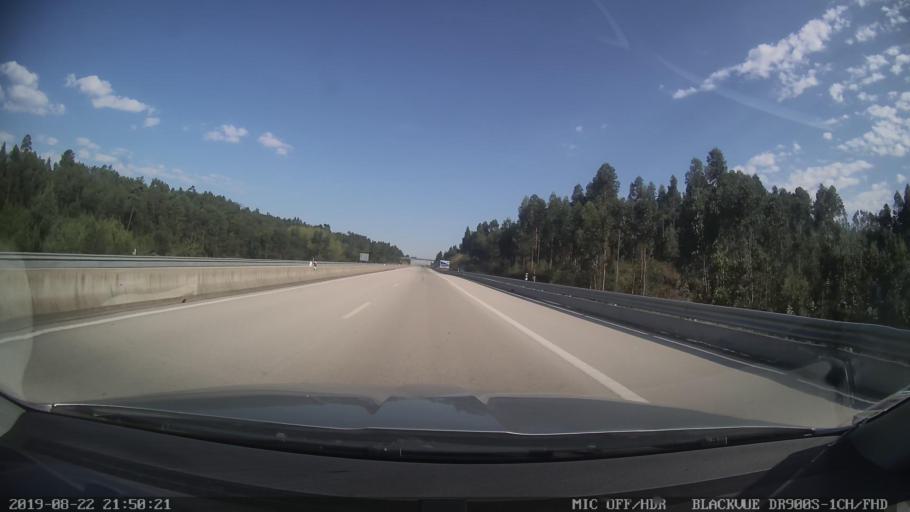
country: PT
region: Coimbra
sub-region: Penela
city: Penela
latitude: 40.0617
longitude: -8.3741
